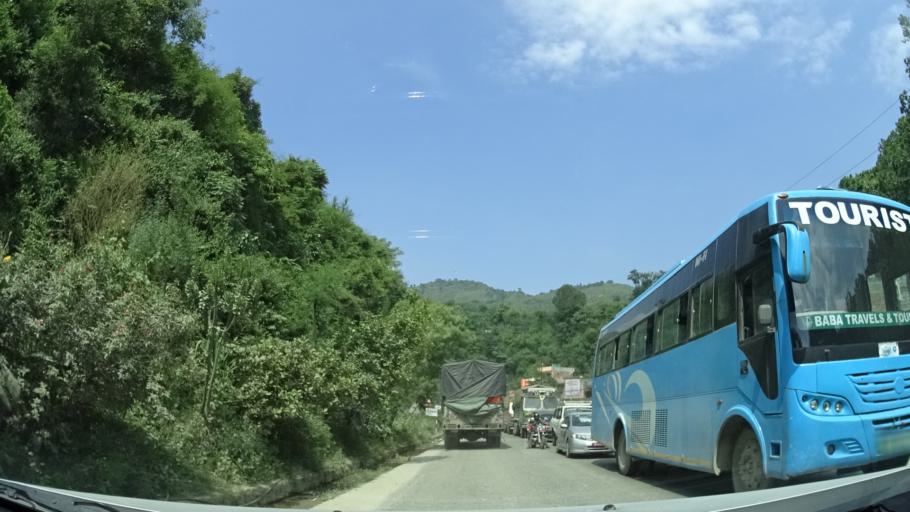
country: NP
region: Central Region
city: Kirtipur
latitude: 27.7990
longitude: 84.9944
